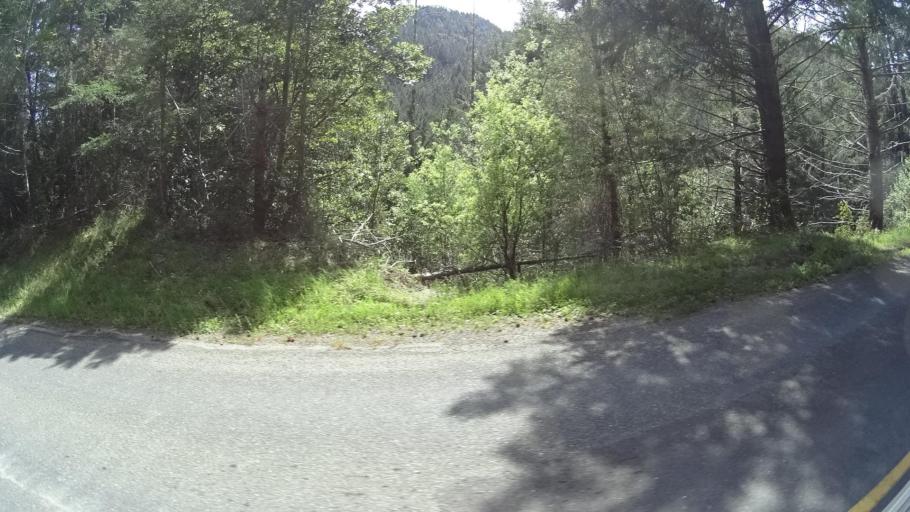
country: US
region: California
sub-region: Humboldt County
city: Rio Dell
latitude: 40.4548
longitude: -123.8014
